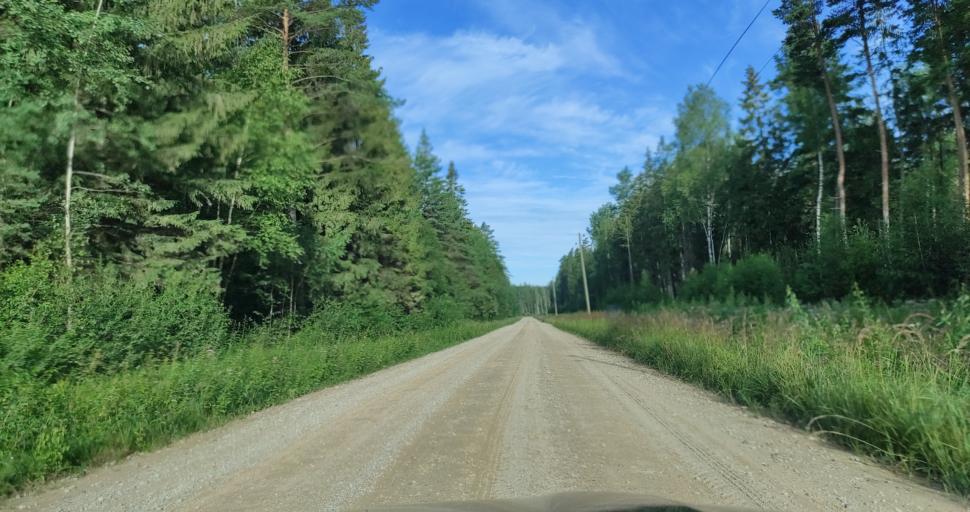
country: LV
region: Durbe
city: Liegi
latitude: 56.7535
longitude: 21.3493
